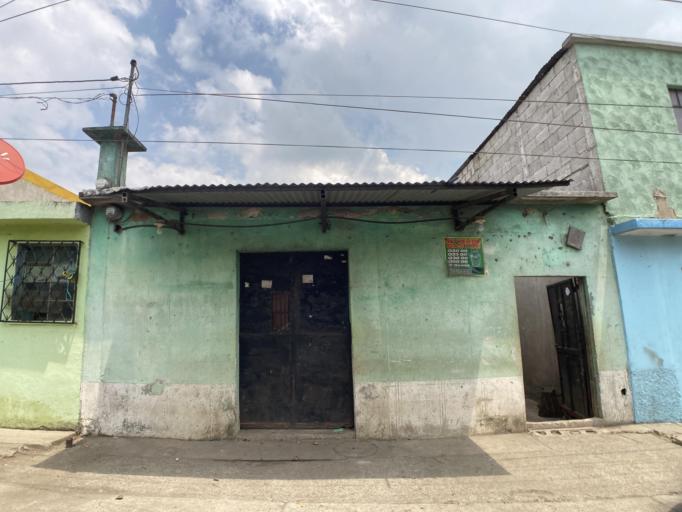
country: GT
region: Guatemala
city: Villa Canales
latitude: 14.4071
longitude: -90.5467
